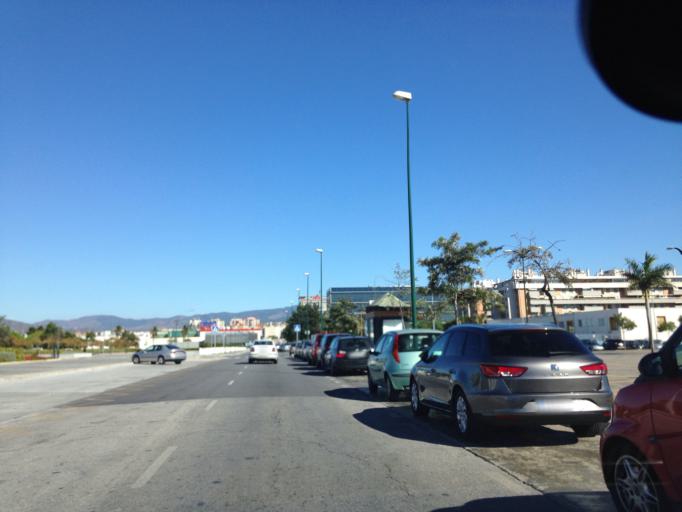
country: ES
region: Andalusia
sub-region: Provincia de Malaga
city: Malaga
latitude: 36.6823
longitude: -4.4594
